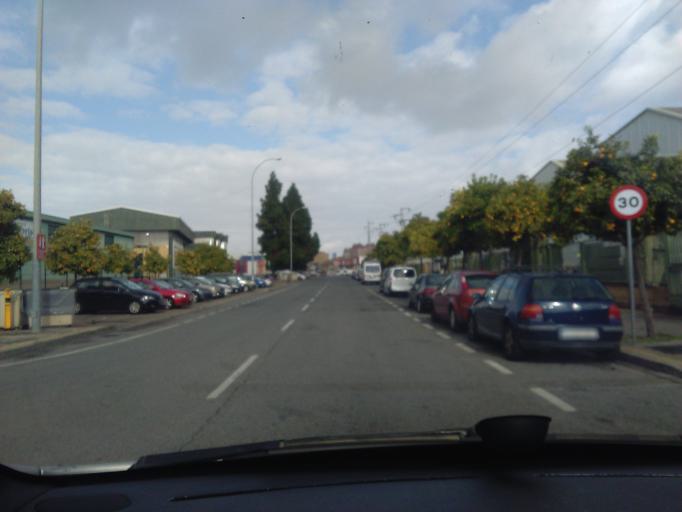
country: ES
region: Andalusia
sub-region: Provincia de Sevilla
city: Sevilla
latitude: 37.3803
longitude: -5.9247
